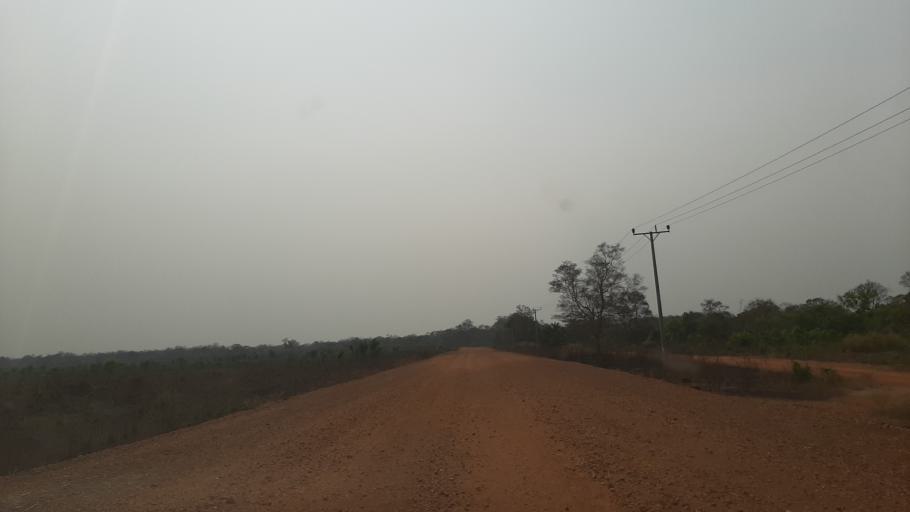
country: ET
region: Gambela
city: Gambela
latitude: 8.1622
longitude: 34.3141
